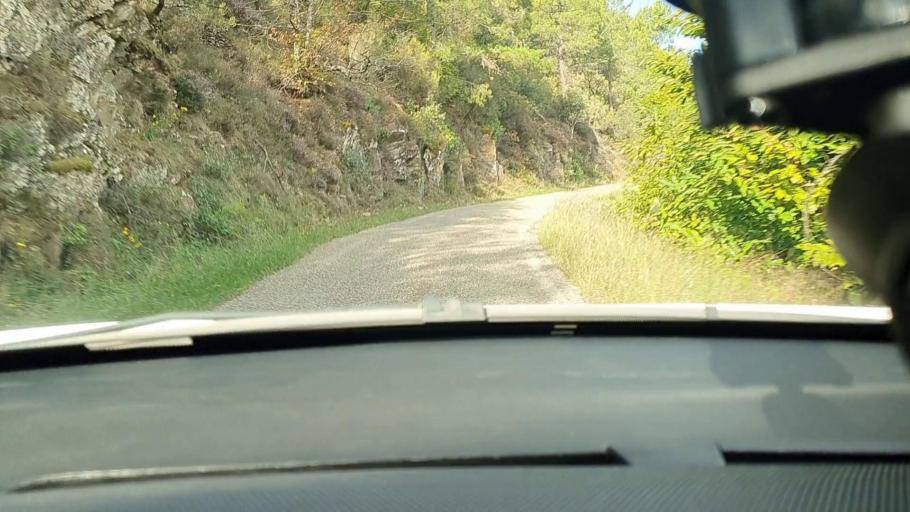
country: FR
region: Languedoc-Roussillon
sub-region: Departement du Gard
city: Besseges
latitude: 44.3248
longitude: 4.0390
